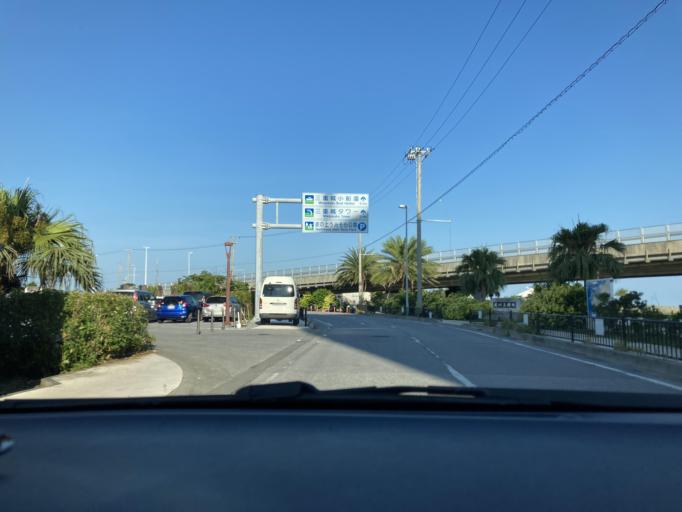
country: JP
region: Okinawa
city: Naha-shi
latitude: 26.2198
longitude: 127.6666
